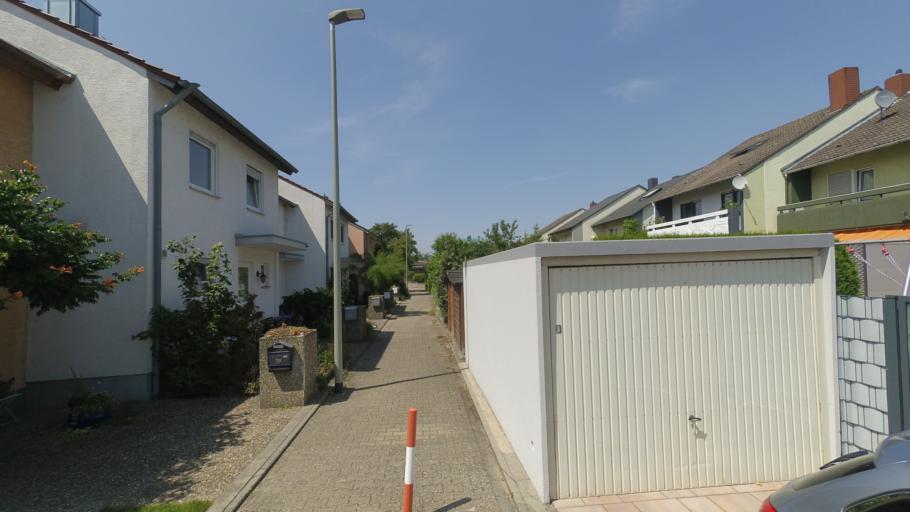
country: DE
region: Rheinland-Pfalz
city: Mutterstadt
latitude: 49.4356
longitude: 8.3662
